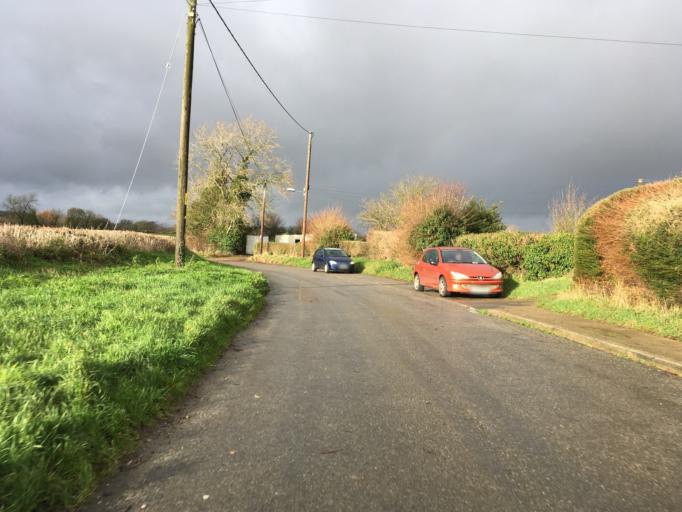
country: GB
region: England
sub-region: Wiltshire
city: Hankerton
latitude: 51.6359
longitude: -2.0706
